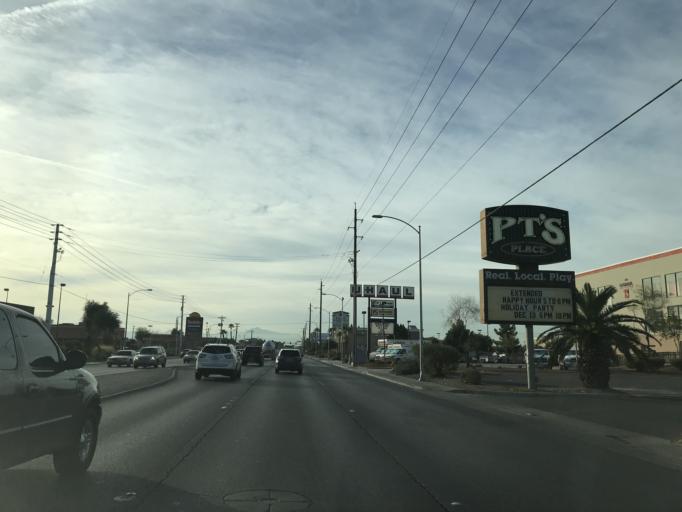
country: US
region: Nevada
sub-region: Clark County
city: Sunrise Manor
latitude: 36.1694
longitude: -115.0622
